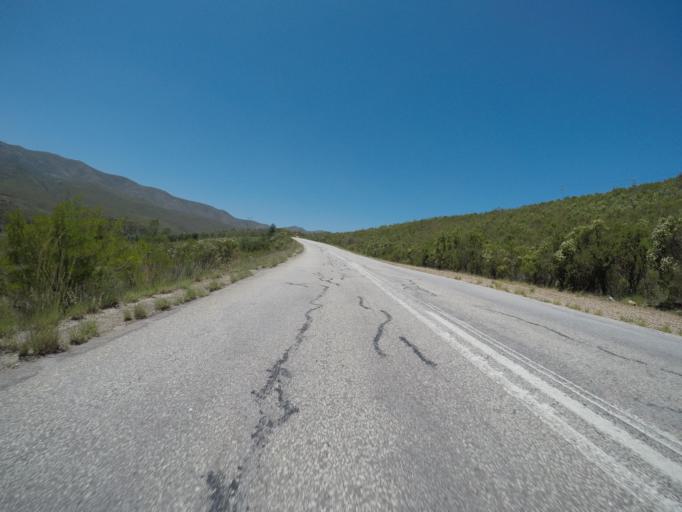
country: ZA
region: Eastern Cape
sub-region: Cacadu District Municipality
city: Kareedouw
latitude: -33.8851
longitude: 24.0728
